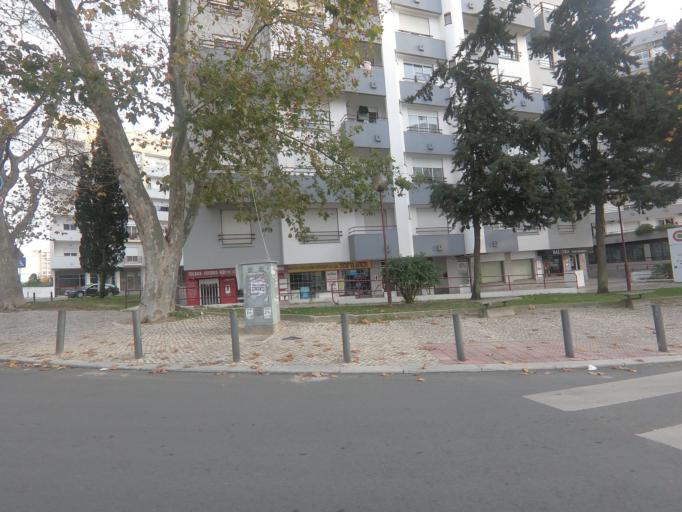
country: PT
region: Setubal
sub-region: Setubal
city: Setubal
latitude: 38.5285
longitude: -8.8824
